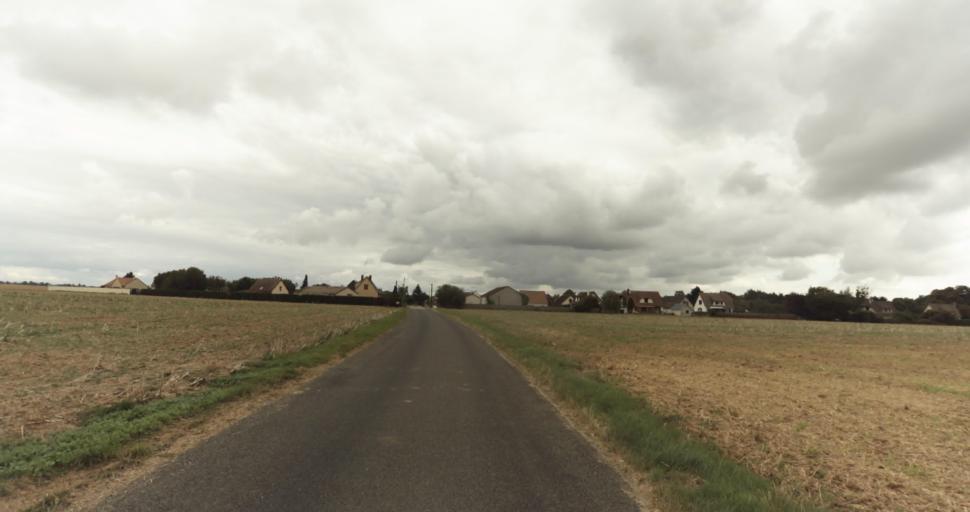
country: FR
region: Haute-Normandie
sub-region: Departement de l'Eure
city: Gravigny
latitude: 49.0163
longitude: 1.2639
